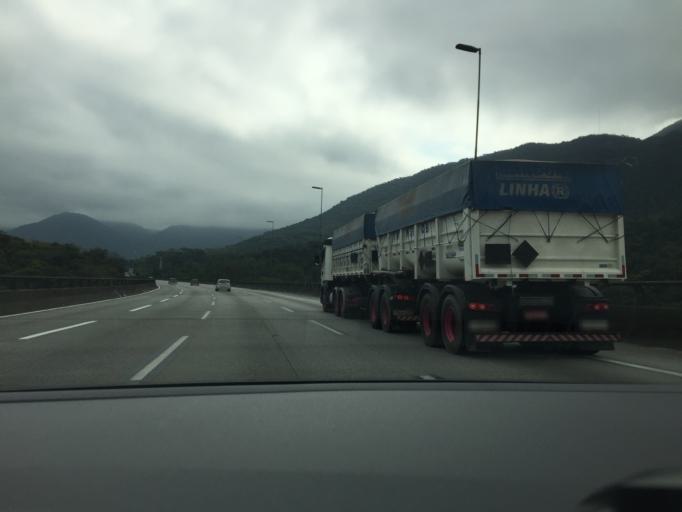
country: BR
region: Sao Paulo
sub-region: Cubatao
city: Cubatao
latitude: -23.8986
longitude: -46.4702
